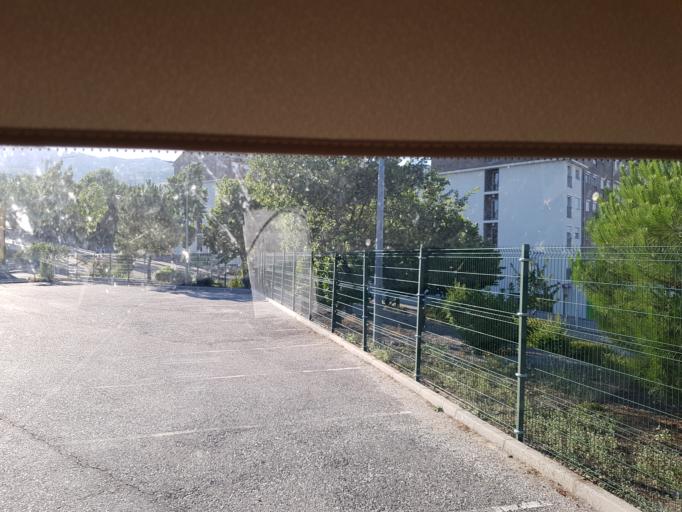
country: PT
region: Castelo Branco
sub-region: Covilha
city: Covilha
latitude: 40.2704
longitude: -7.4927
